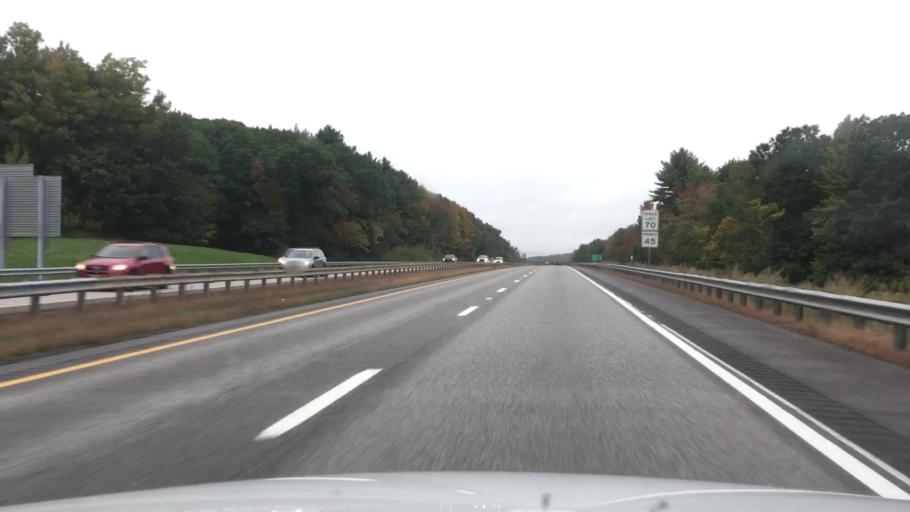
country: US
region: Maine
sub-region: Cumberland County
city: Falmouth
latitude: 43.7413
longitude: -70.3024
